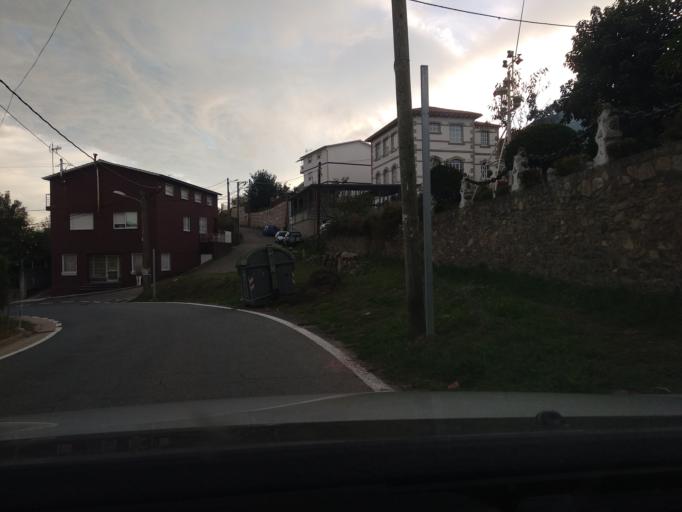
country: ES
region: Galicia
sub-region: Provincia de Pontevedra
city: Moana
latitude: 42.2882
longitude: -8.6856
